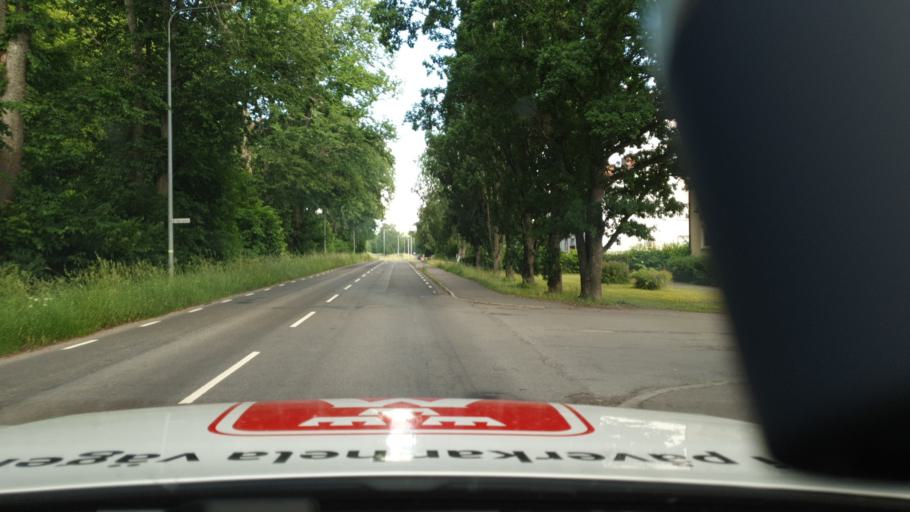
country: SE
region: Vaestra Goetaland
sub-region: Skara Kommun
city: Axvall
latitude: 58.3879
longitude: 13.5774
